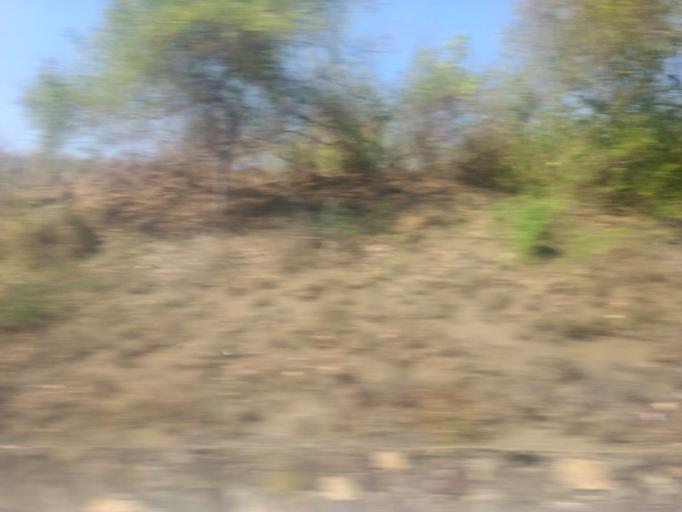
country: MX
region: Colima
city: Armeria
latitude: 18.9446
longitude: -104.1127
